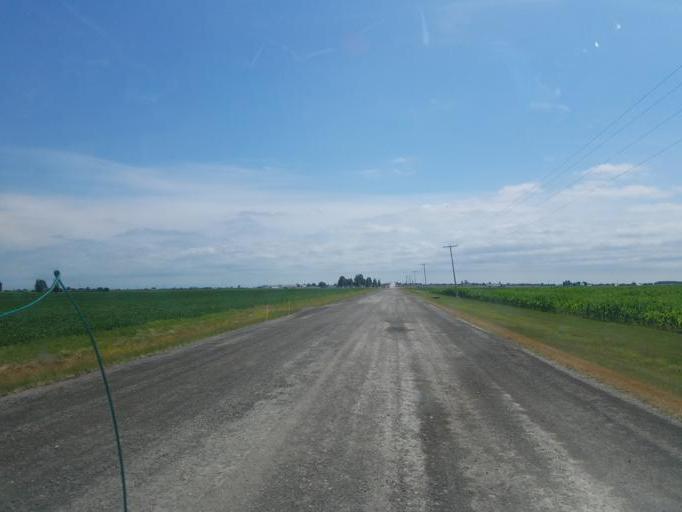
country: US
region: Indiana
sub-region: Allen County
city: Woodburn
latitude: 41.1602
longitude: -84.8489
